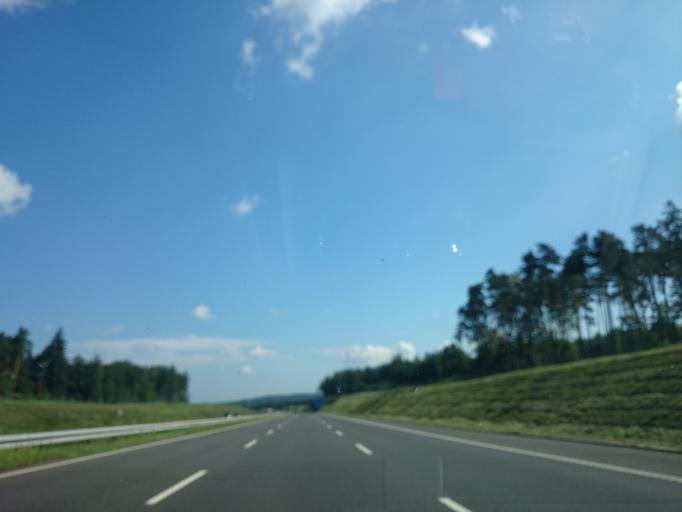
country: PL
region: Silesian Voivodeship
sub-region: Powiat rybnicki
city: Stanowice
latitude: 50.1149
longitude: 18.6803
